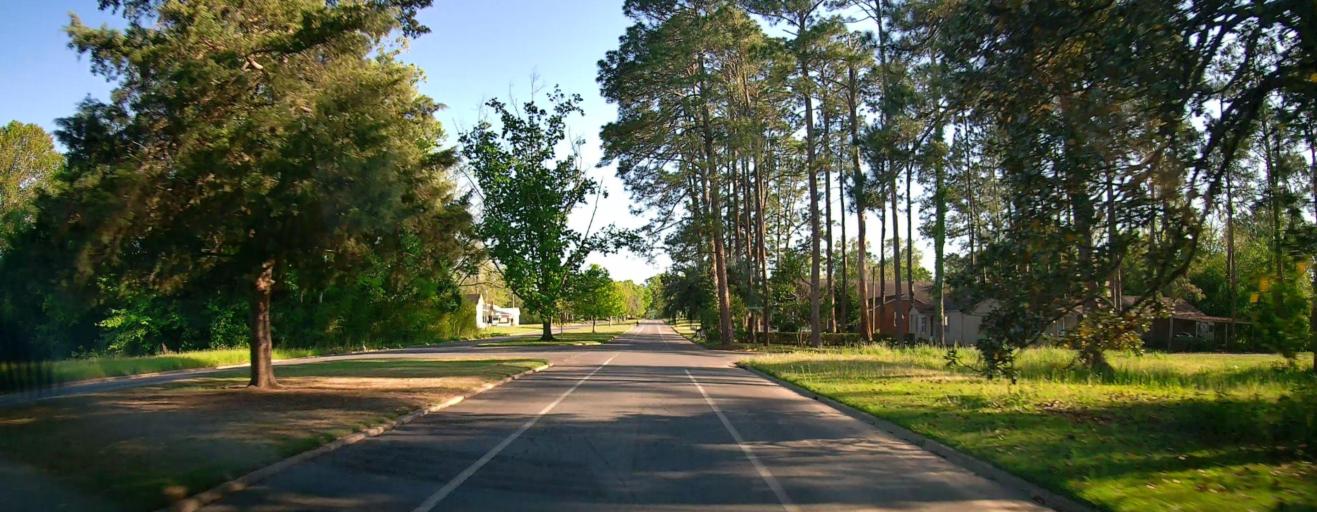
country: US
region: Georgia
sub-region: Ben Hill County
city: Fitzgerald
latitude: 31.7221
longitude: -83.2547
